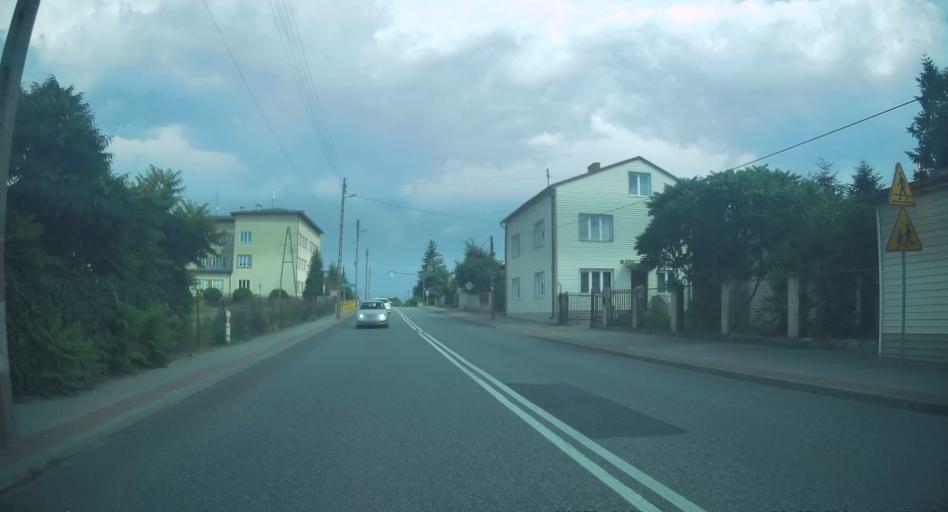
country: PL
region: Lodz Voivodeship
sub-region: Powiat brzezinski
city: Jezow
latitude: 51.8131
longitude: 19.9719
